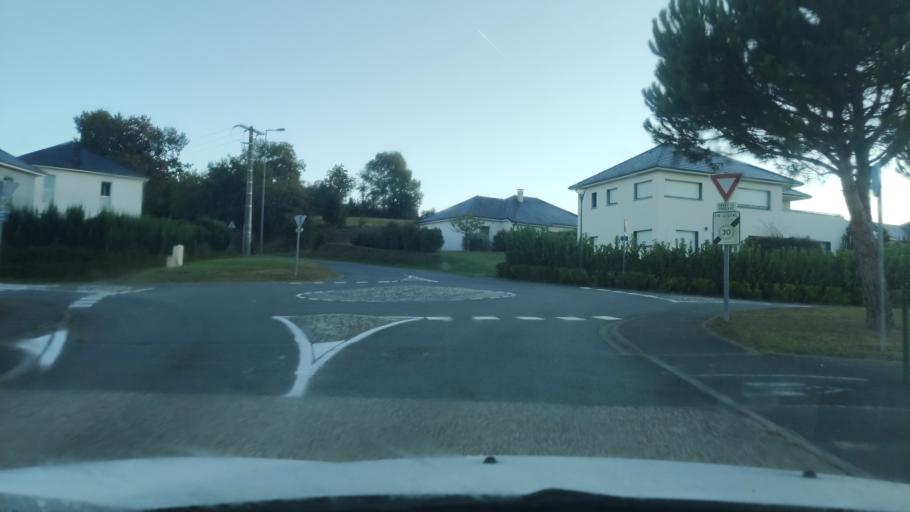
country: FR
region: Aquitaine
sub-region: Departement des Pyrenees-Atlantiques
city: Sauvagnon
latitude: 43.3998
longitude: -0.3841
